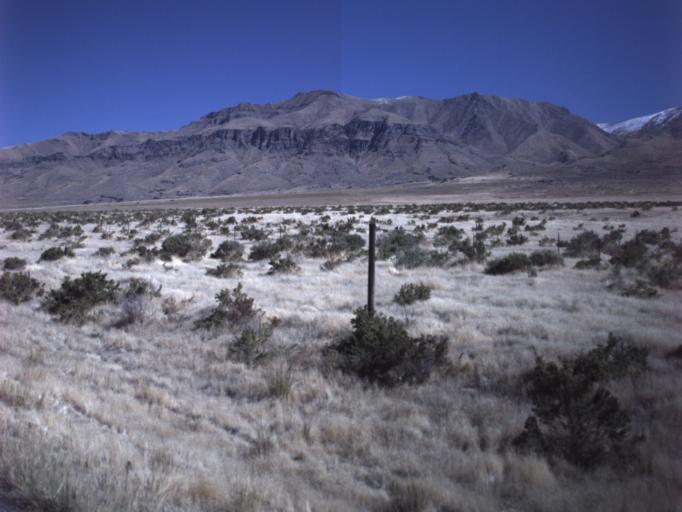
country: US
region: Utah
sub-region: Tooele County
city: Grantsville
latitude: 40.6224
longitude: -112.6996
